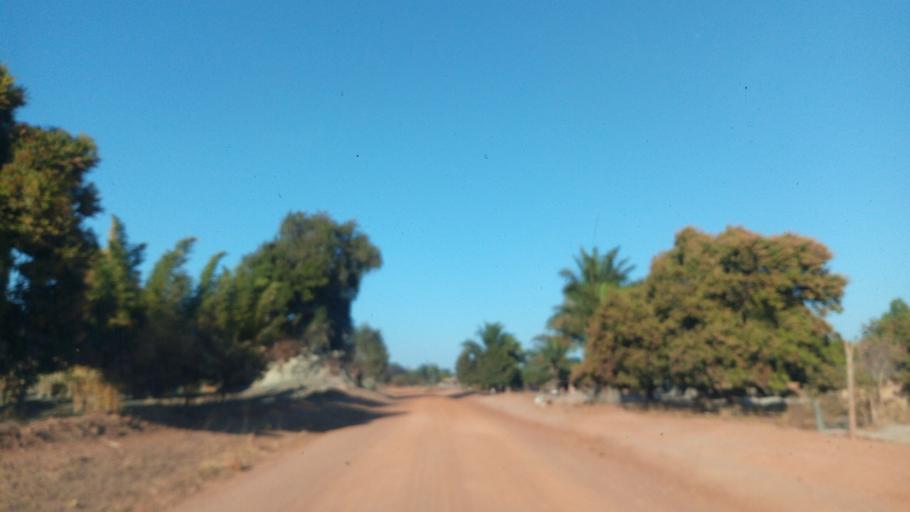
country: ZM
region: Luapula
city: Mwense
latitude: -10.4687
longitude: 28.5181
